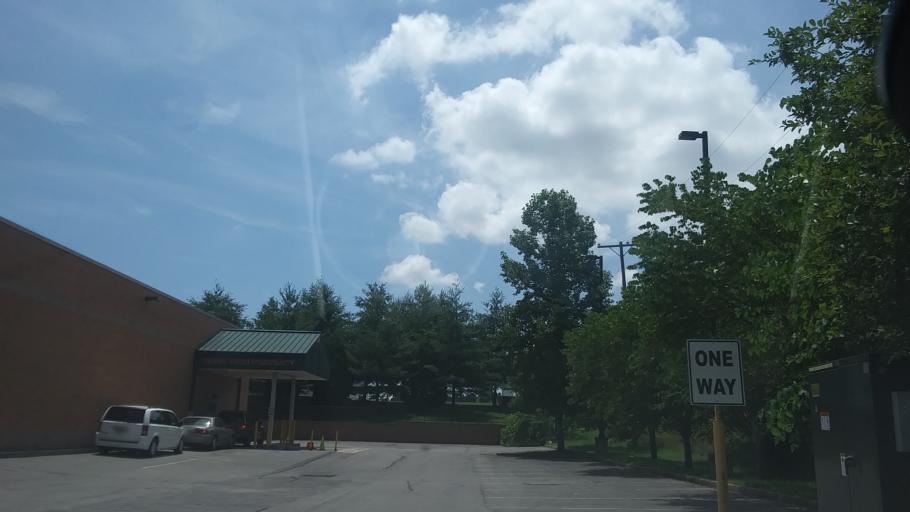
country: US
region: Tennessee
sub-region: Rutherford County
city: La Vergne
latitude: 36.0639
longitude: -86.6289
